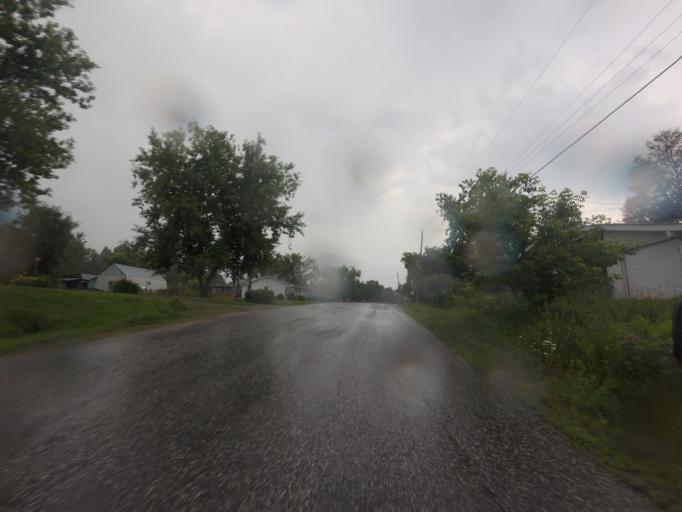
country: CA
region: Quebec
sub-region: Outaouais
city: Maniwaki
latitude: 46.4111
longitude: -75.9577
